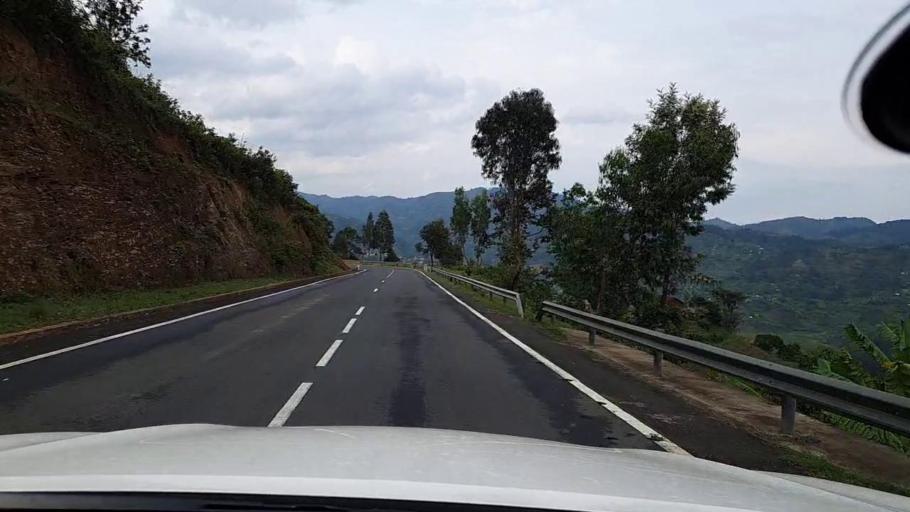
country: RW
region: Western Province
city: Kibuye
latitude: -2.1841
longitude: 29.2902
